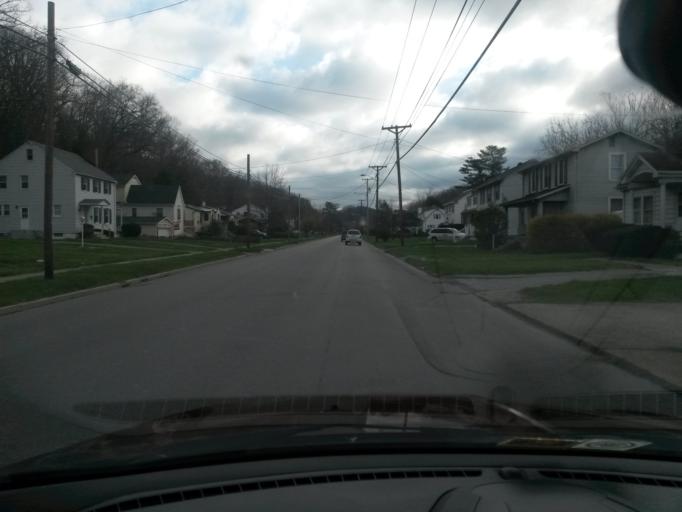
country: US
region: West Virginia
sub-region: Mercer County
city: Bluefield
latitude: 37.2471
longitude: -81.2408
